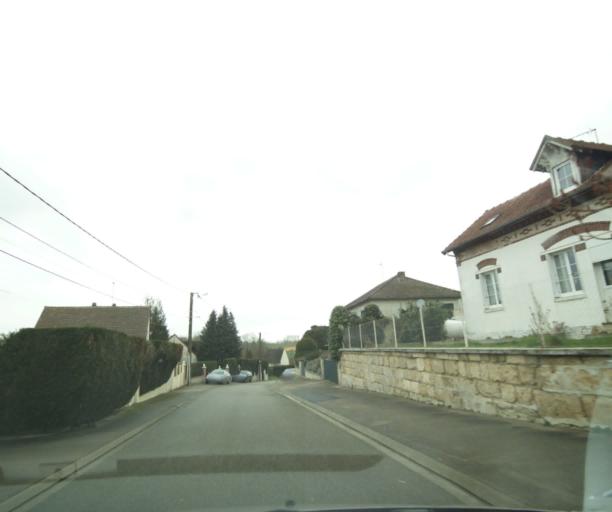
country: FR
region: Picardie
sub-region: Departement de l'Oise
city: Noyon
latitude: 49.5908
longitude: 3.0159
